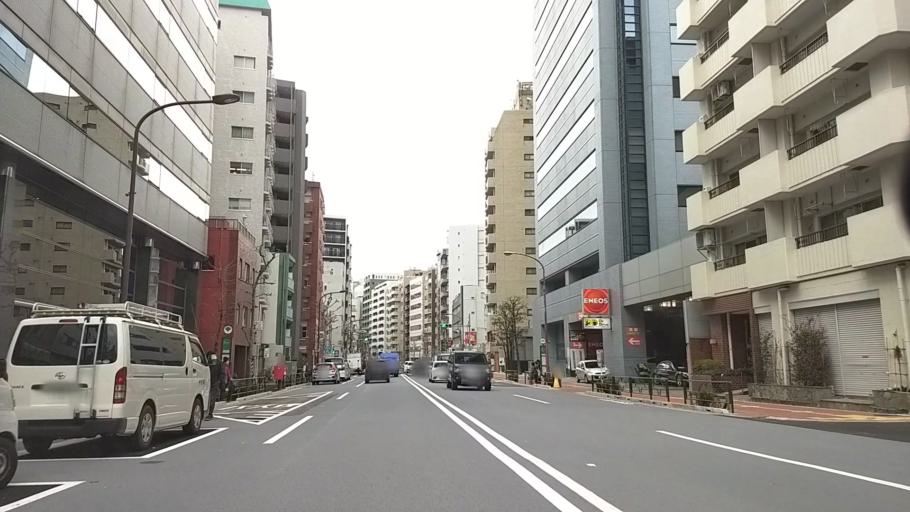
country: JP
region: Tokyo
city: Tokyo
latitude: 35.6248
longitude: 139.7312
